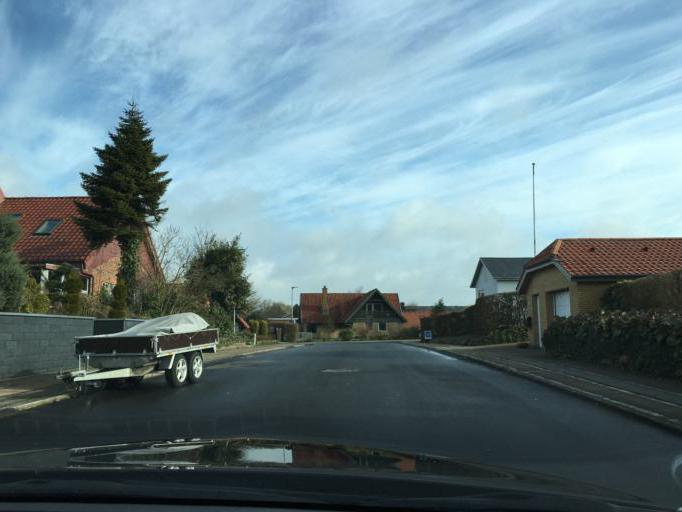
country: DK
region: South Denmark
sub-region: Kolding Kommune
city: Kolding
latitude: 55.4990
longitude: 9.4487
